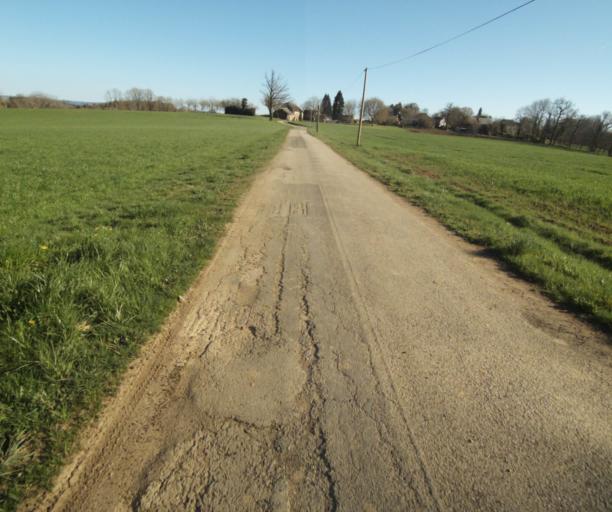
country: FR
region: Limousin
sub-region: Departement de la Correze
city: Seilhac
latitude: 45.3881
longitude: 1.7333
